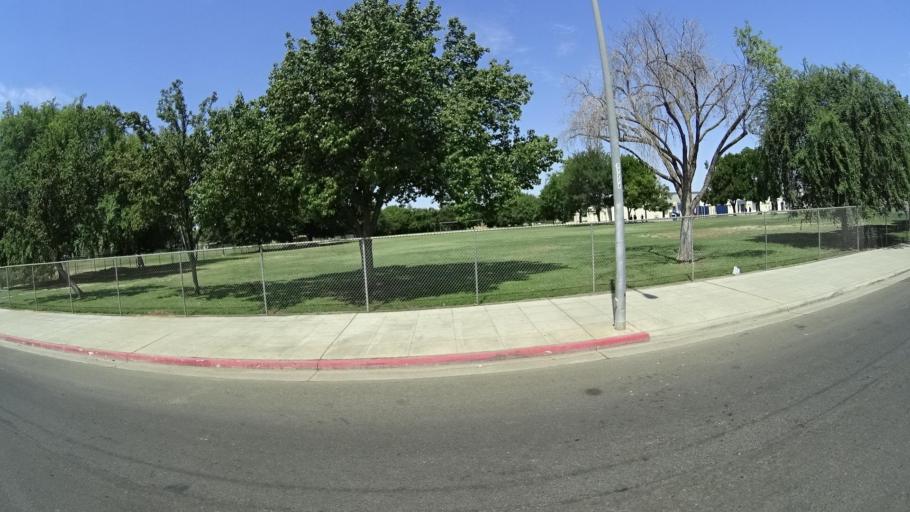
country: US
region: California
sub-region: Fresno County
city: Sunnyside
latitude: 36.7298
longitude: -119.7139
